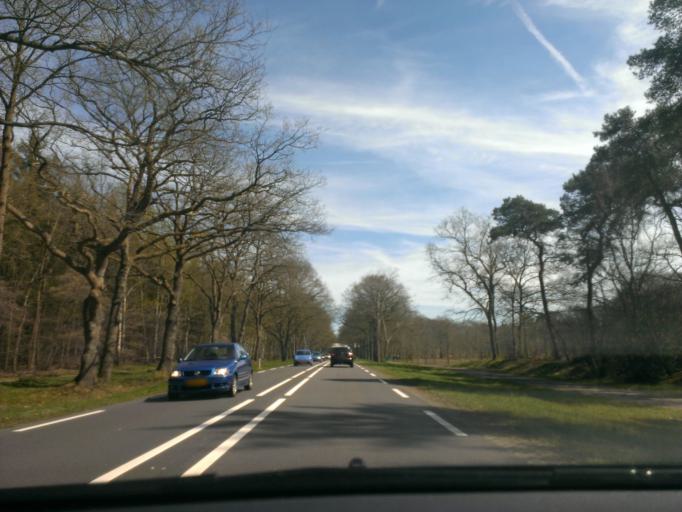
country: NL
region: Overijssel
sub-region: Gemeente Twenterand
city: Den Ham
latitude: 52.3683
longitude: 6.4150
